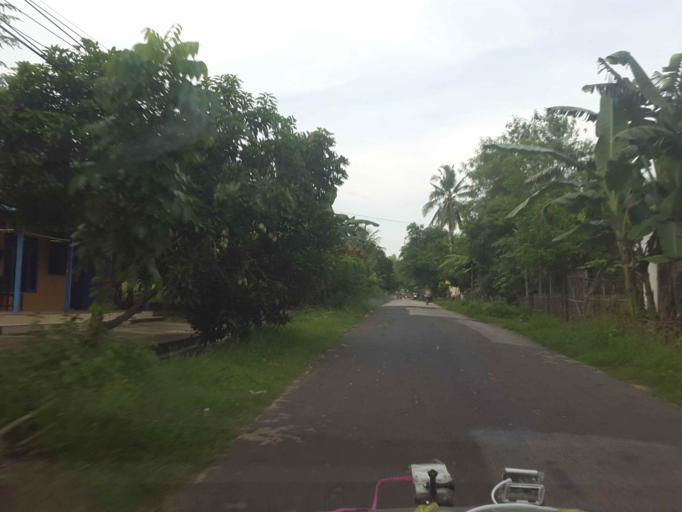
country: ID
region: East Java
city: Giring Barat
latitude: -6.9689
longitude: 113.8682
